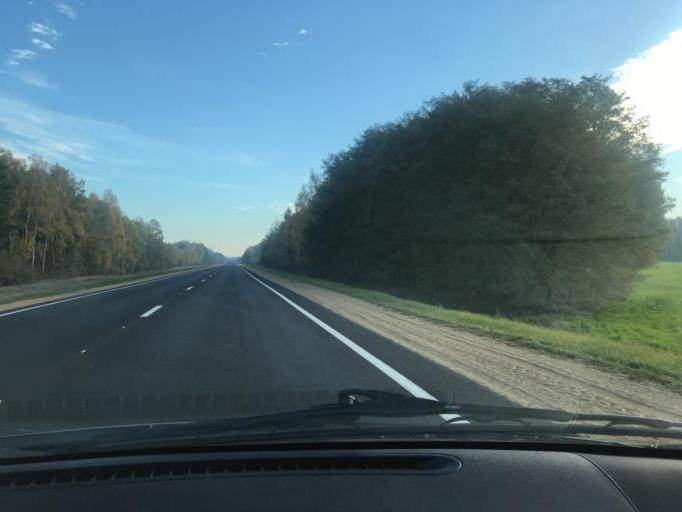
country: BY
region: Brest
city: Drahichyn
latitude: 52.2184
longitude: 25.1090
